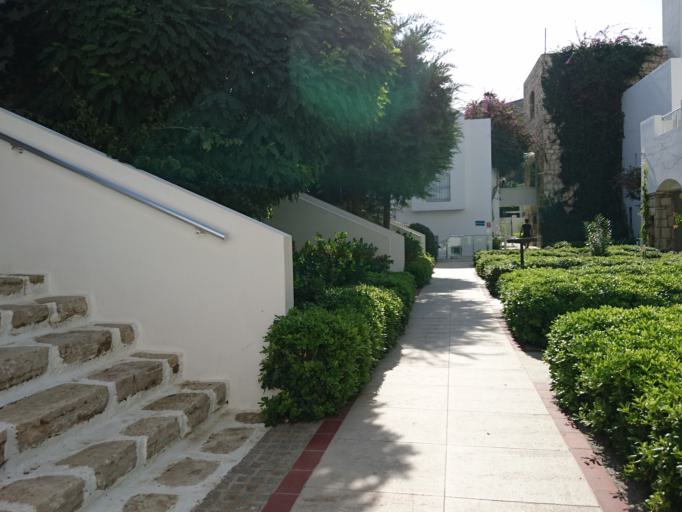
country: TR
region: Mugla
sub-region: Bodrum
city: Bodrum
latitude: 37.0286
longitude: 27.4157
